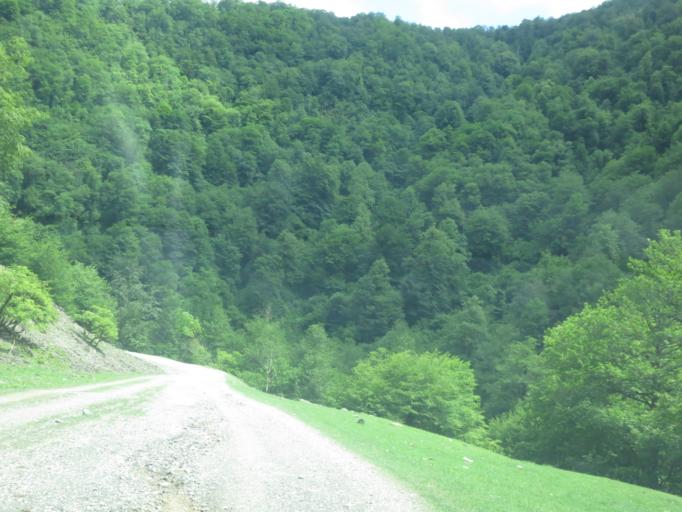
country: GE
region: Kakheti
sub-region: Telavi
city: Telavi
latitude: 42.1943
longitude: 45.4607
